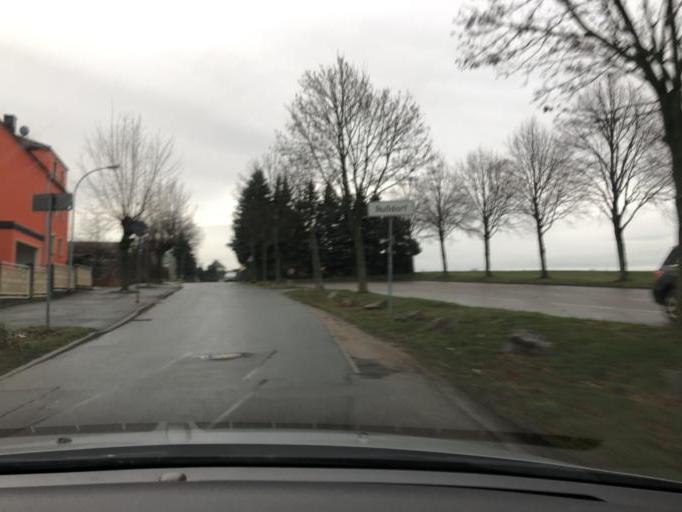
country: DE
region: Saxony
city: Limbach-Oberfrohna
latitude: 50.8544
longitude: 12.7280
